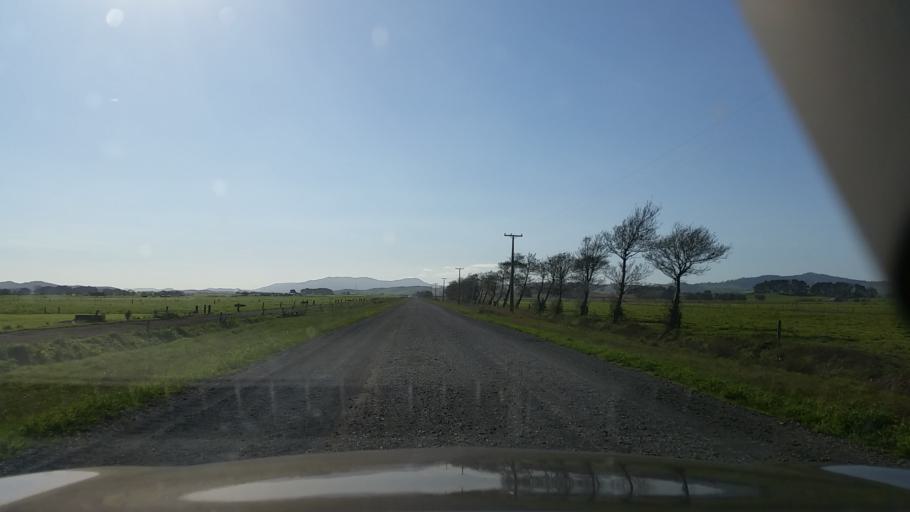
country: NZ
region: Waikato
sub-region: Hamilton City
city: Hamilton
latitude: -37.6443
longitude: 175.4324
